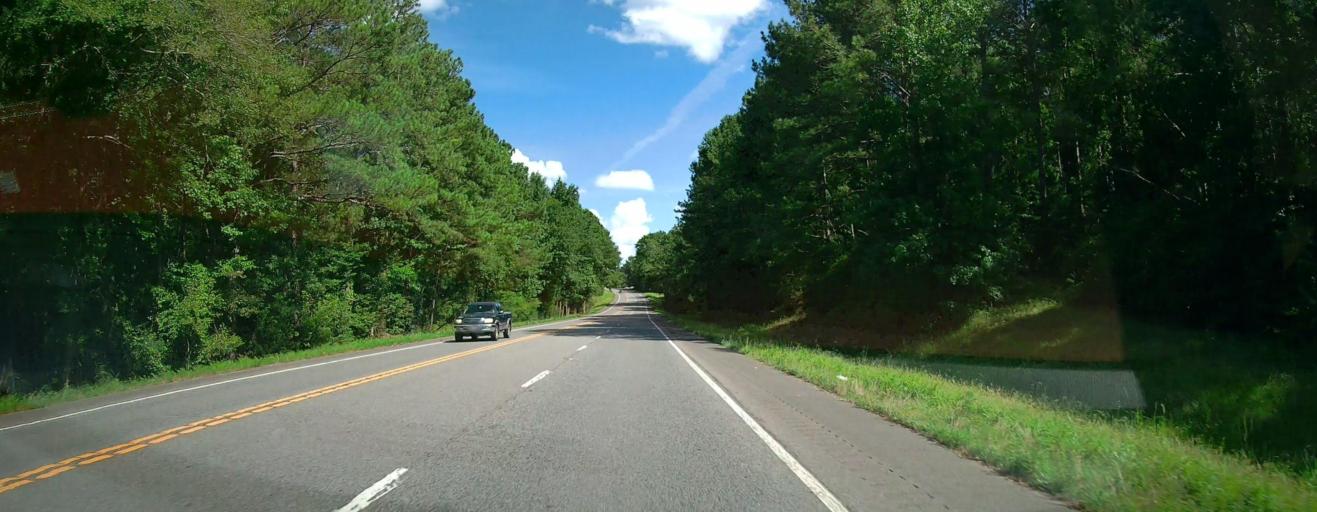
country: US
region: Alabama
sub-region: Pickens County
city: Gordo
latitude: 33.2948
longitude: -87.8750
